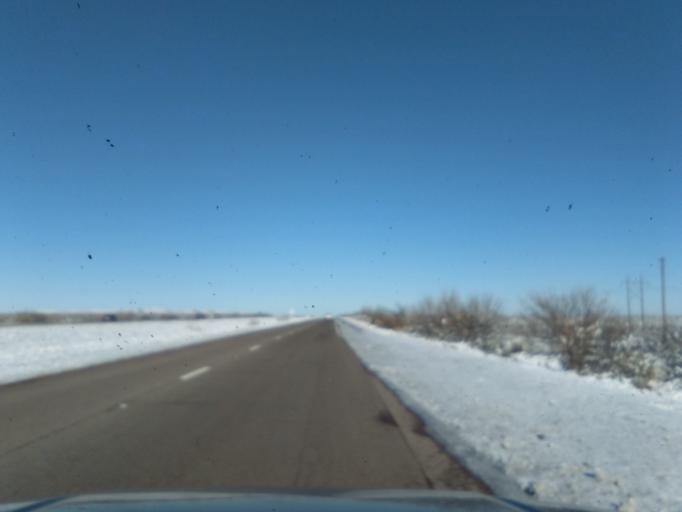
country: US
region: New Mexico
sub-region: Socorro County
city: Socorro
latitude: 33.6390
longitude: -107.1181
